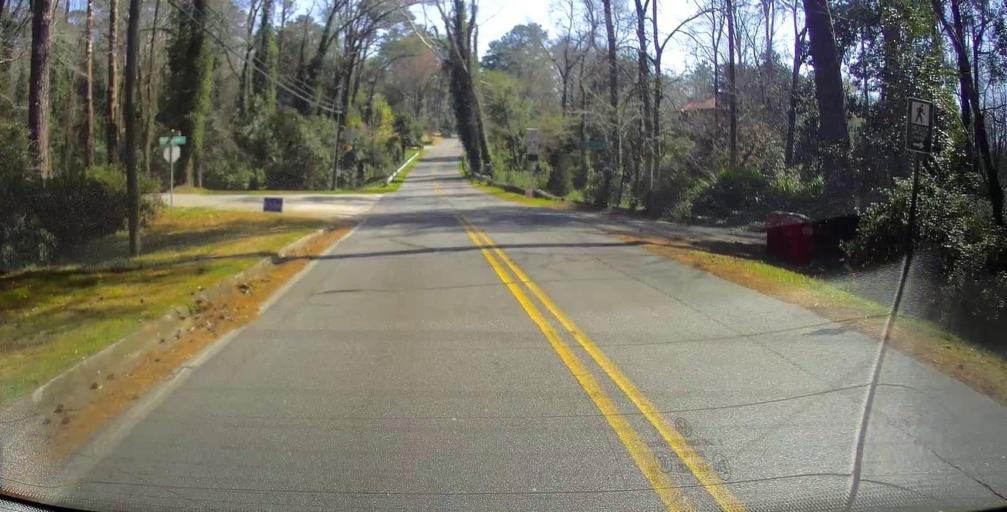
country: US
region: Georgia
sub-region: Bibb County
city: Macon
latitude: 32.8571
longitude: -83.6317
